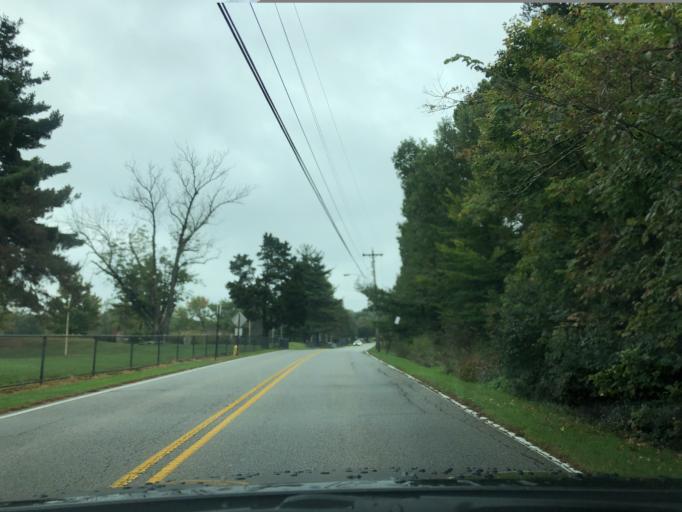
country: US
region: Ohio
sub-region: Hamilton County
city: Sharonville
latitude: 39.2856
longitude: -84.3860
